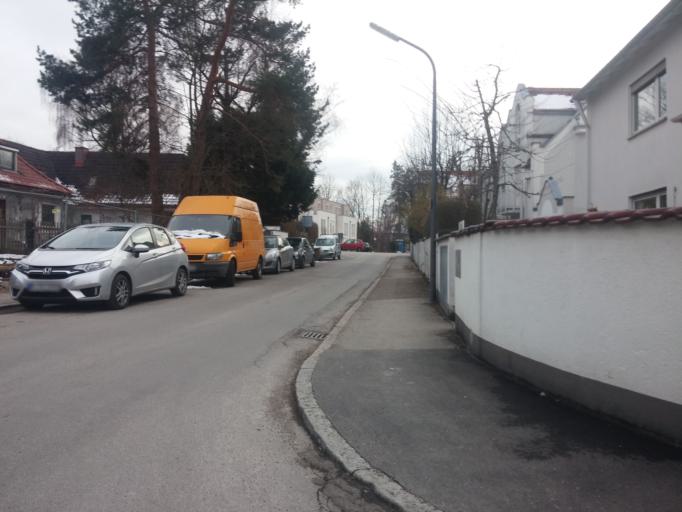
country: DE
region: Bavaria
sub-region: Upper Bavaria
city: Neubiberg
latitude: 48.1215
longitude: 11.6749
